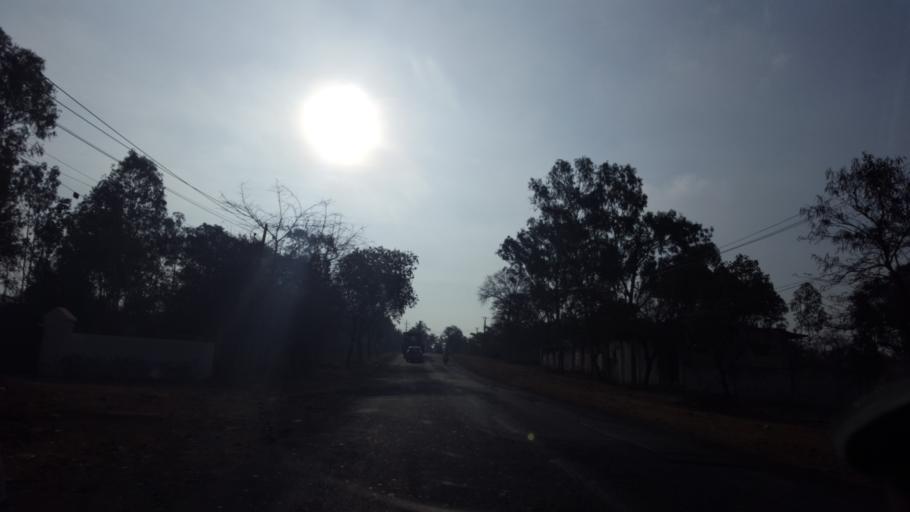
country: IN
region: Karnataka
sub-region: Bangalore Urban
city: Bangalore
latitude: 12.9062
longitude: 77.5011
